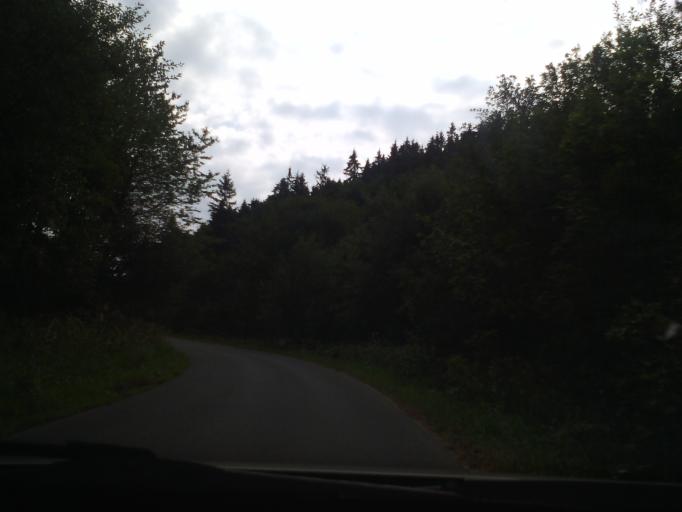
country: CZ
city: Mezimesti
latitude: 50.6904
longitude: 16.2724
